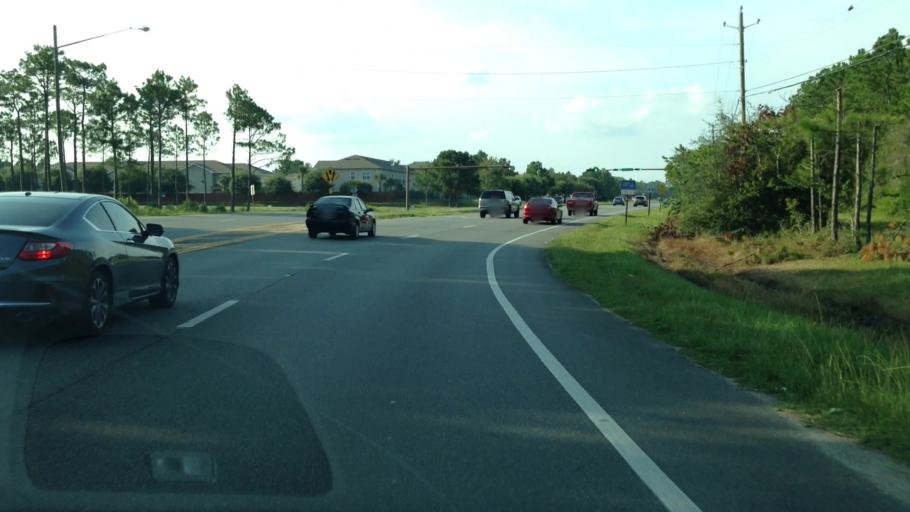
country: US
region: Florida
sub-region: Okaloosa County
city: Mary Esther
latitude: 30.4281
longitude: -86.6673
